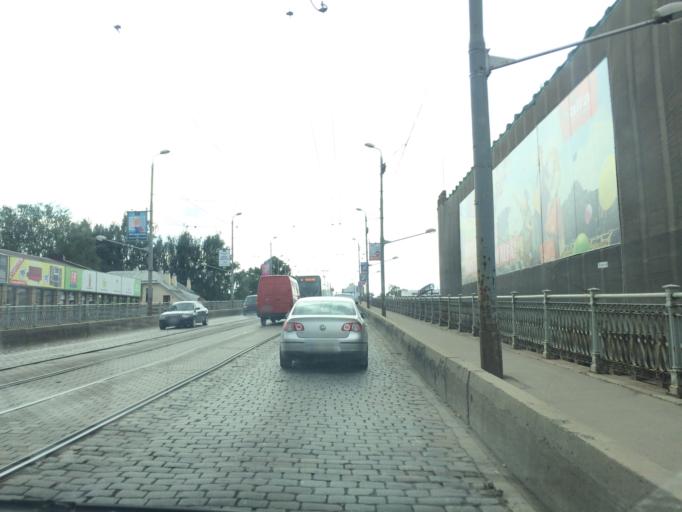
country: LV
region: Riga
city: Riga
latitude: 56.9701
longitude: 24.1564
